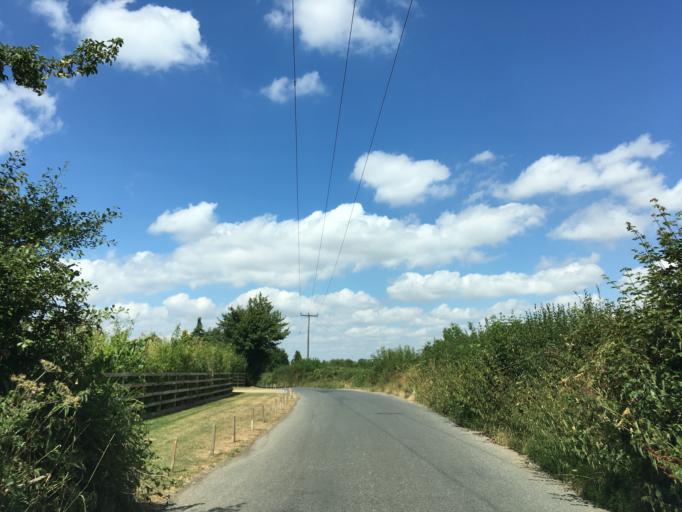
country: GB
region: England
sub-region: Gloucestershire
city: Shurdington
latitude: 51.8526
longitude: -2.1294
